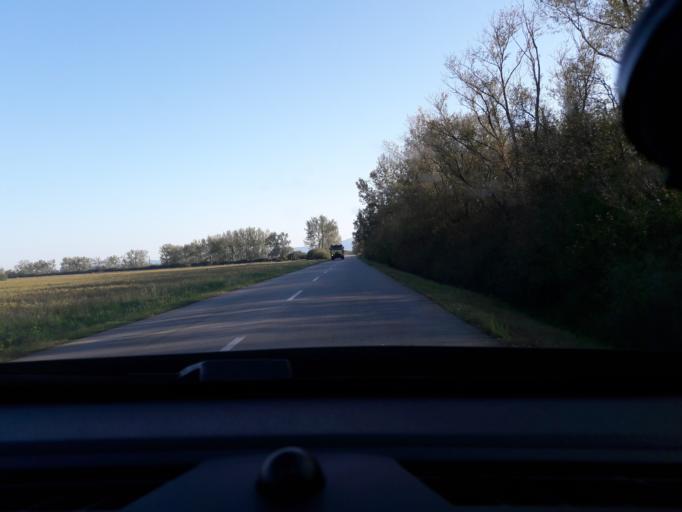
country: SK
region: Kosicky
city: Michalovce
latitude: 48.6519
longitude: 21.9382
